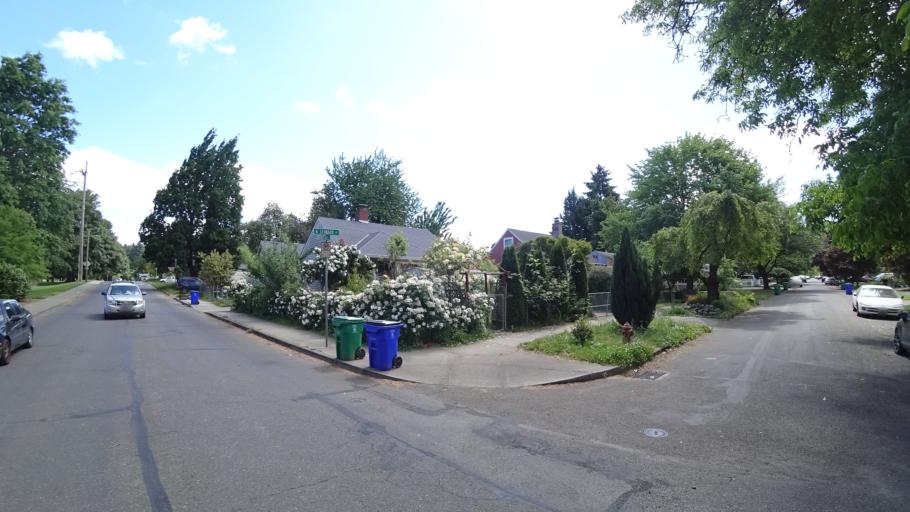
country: US
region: Oregon
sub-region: Washington County
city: West Haven
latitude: 45.6016
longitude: -122.7622
